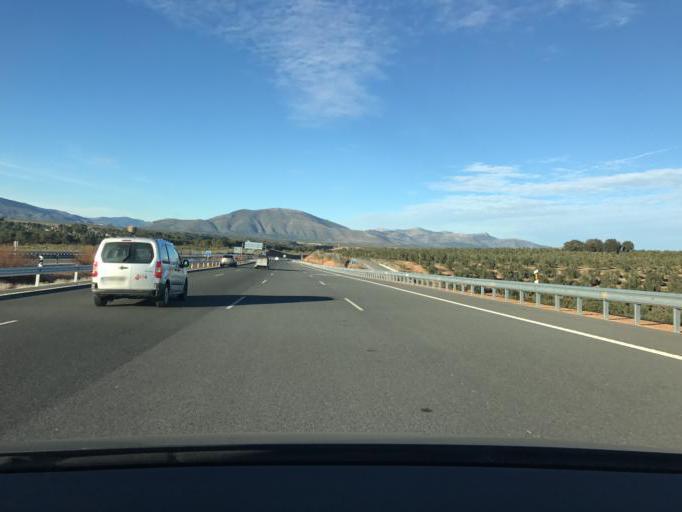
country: ES
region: Andalusia
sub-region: Provincia de Granada
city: Albolote
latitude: 37.2722
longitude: -3.6580
